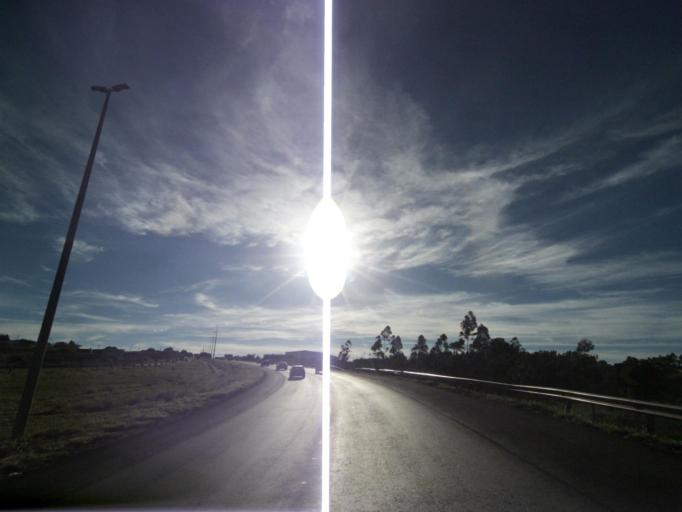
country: BR
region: Federal District
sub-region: Brasilia
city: Brasilia
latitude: -15.7896
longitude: -48.2254
